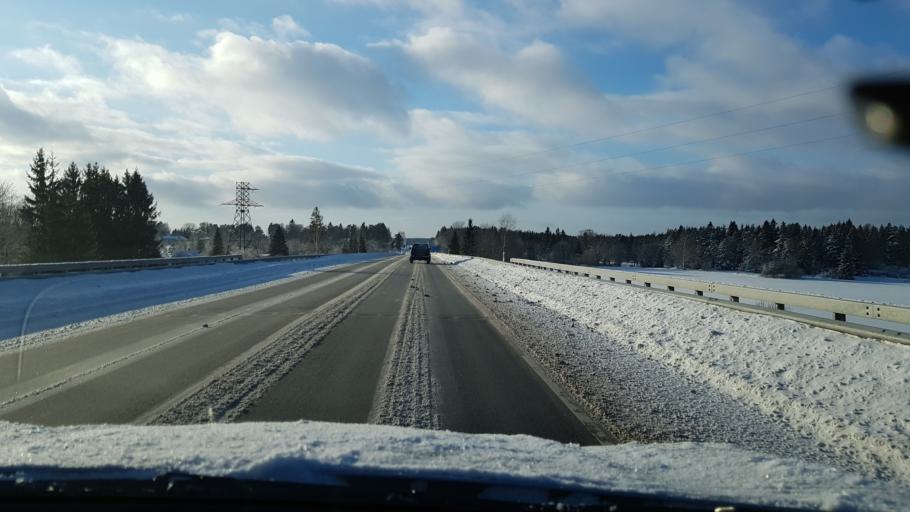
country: EE
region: Harju
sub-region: Nissi vald
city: Riisipere
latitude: 59.1273
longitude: 24.3137
